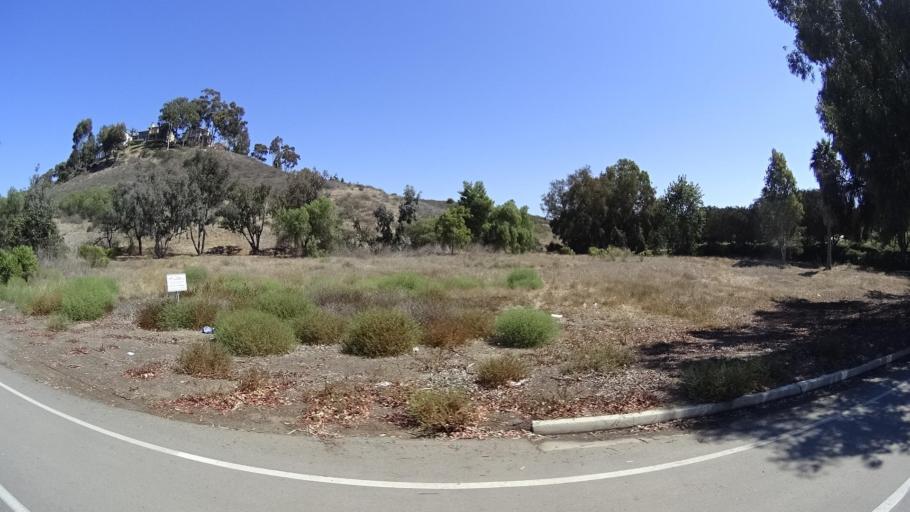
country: US
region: California
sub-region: San Diego County
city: Fairbanks Ranch
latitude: 32.9813
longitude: -117.2055
